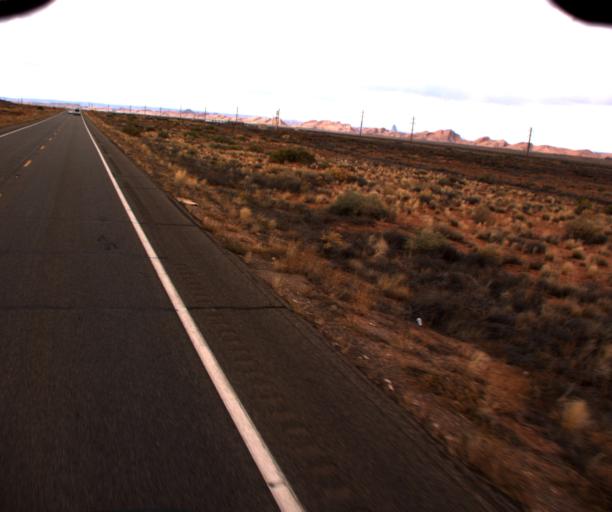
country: US
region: Arizona
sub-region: Navajo County
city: Kayenta
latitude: 36.7778
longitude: -110.0065
